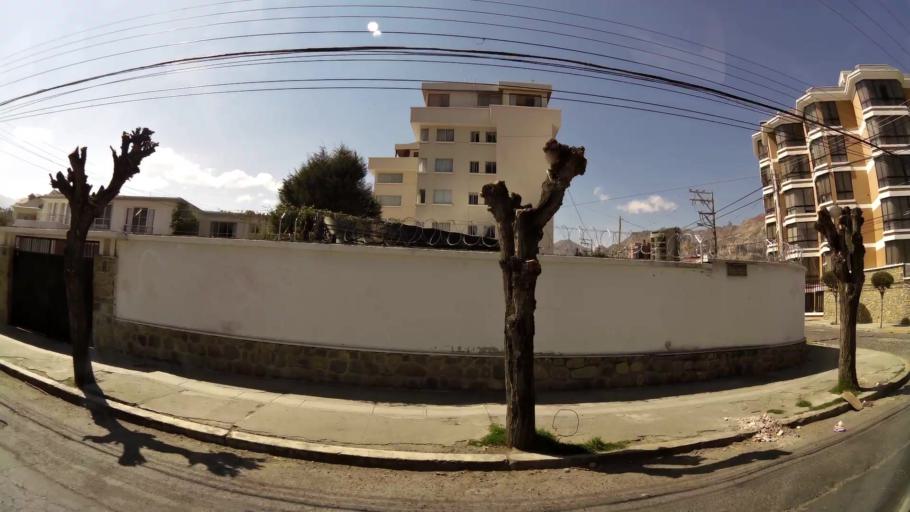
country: BO
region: La Paz
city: La Paz
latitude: -16.5429
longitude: -68.0832
